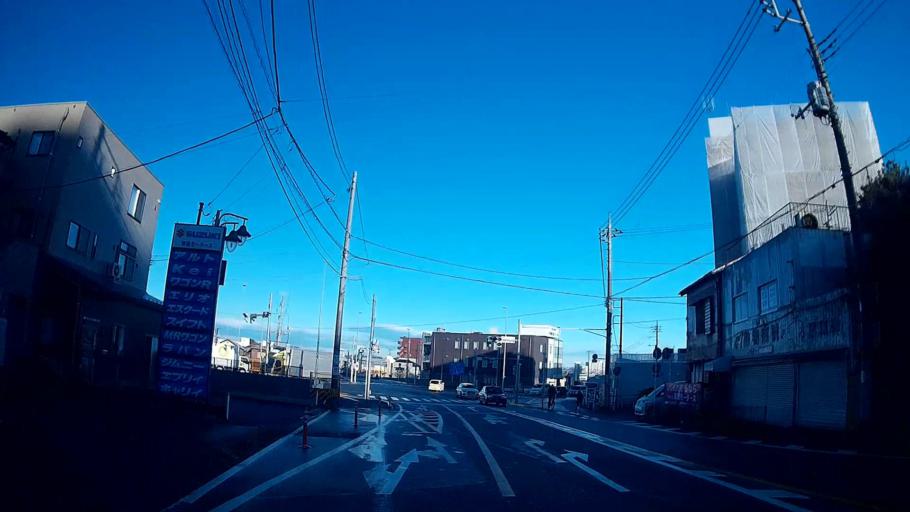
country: JP
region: Saitama
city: Sayama
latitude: 35.8416
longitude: 139.3866
